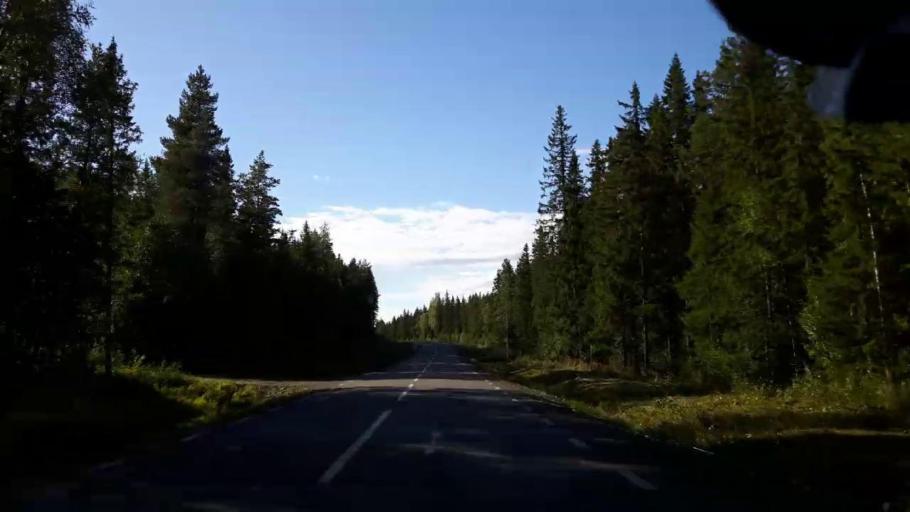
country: SE
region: Jaemtland
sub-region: Ragunda Kommun
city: Hammarstrand
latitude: 63.5354
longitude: 16.0392
